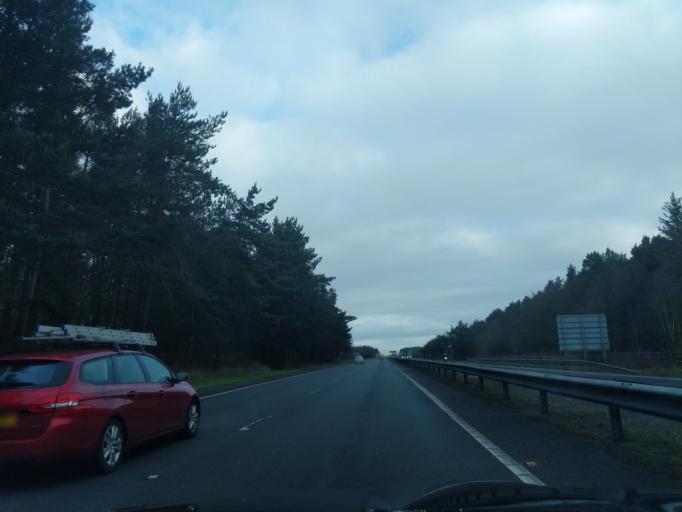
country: GB
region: England
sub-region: Newcastle upon Tyne
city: Hazlerigg
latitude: 55.0711
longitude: -1.6405
